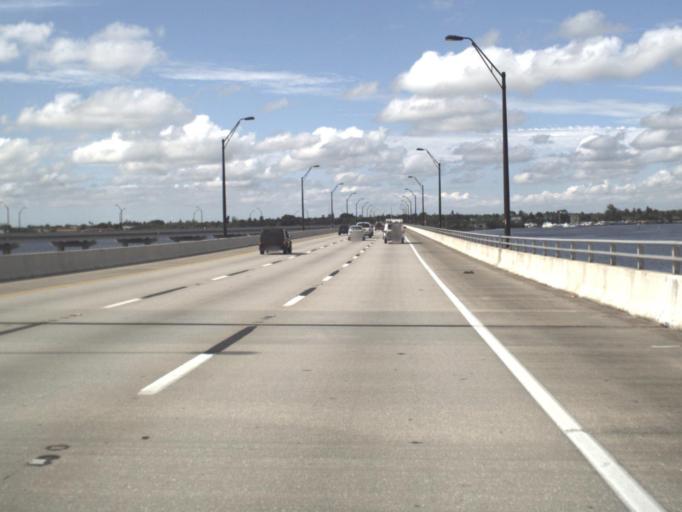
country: US
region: Florida
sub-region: Lee County
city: North Fort Myers
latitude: 26.6548
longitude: -81.8694
